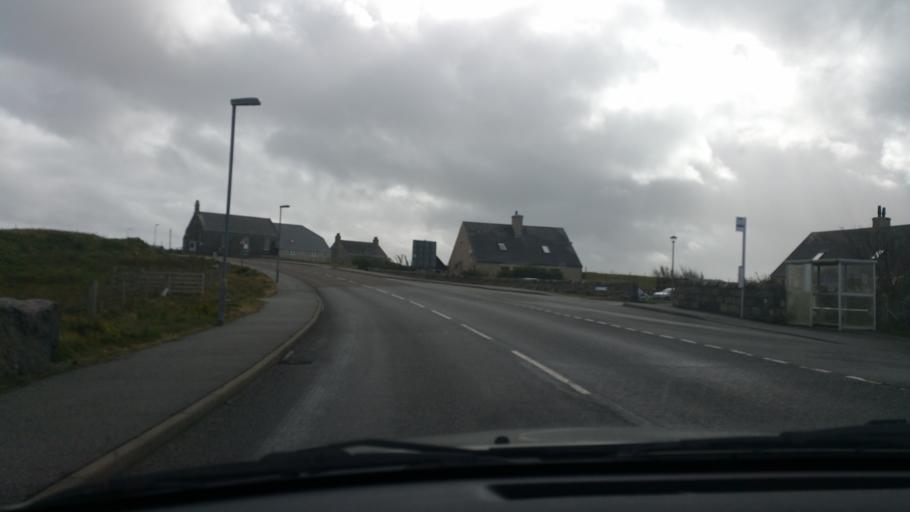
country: GB
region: Scotland
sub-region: Eilean Siar
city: Isle of North Uist
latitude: 57.5528
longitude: -7.3342
